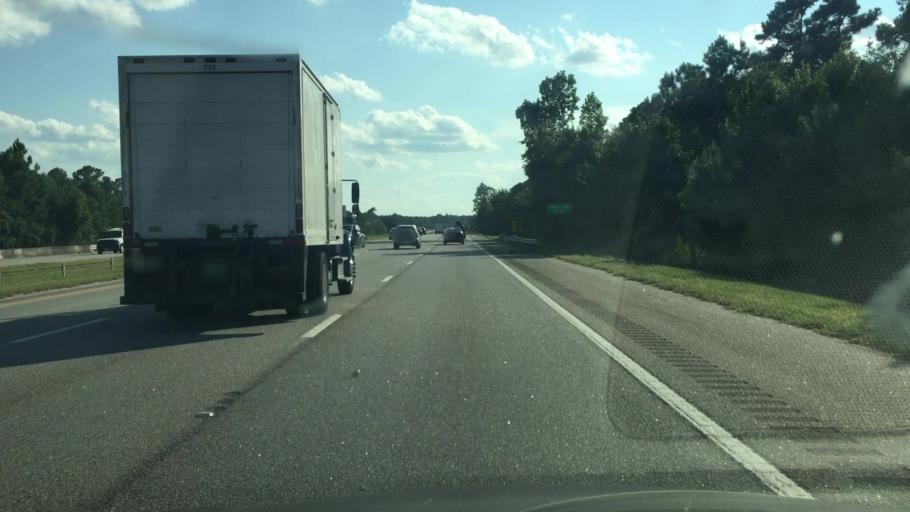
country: US
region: South Carolina
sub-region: Horry County
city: North Myrtle Beach
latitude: 33.8329
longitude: -78.7149
